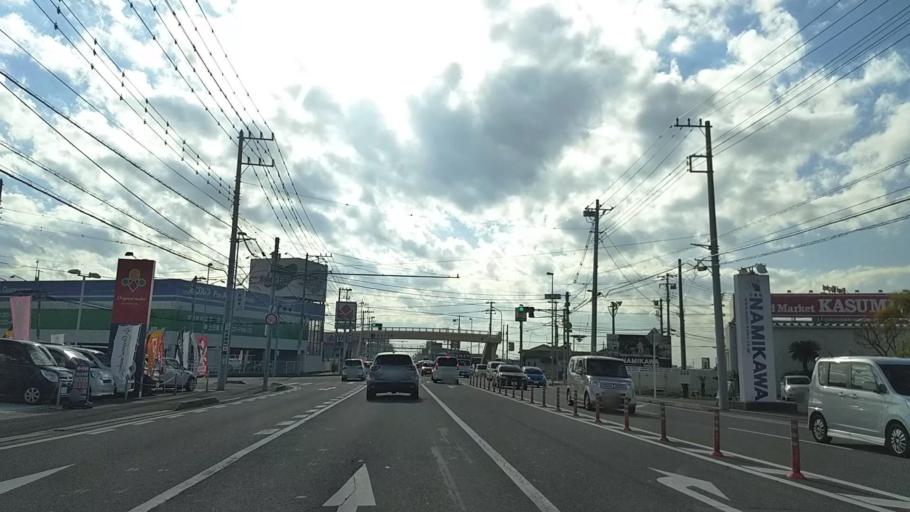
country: JP
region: Chiba
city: Togane
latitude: 35.5769
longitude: 140.3819
